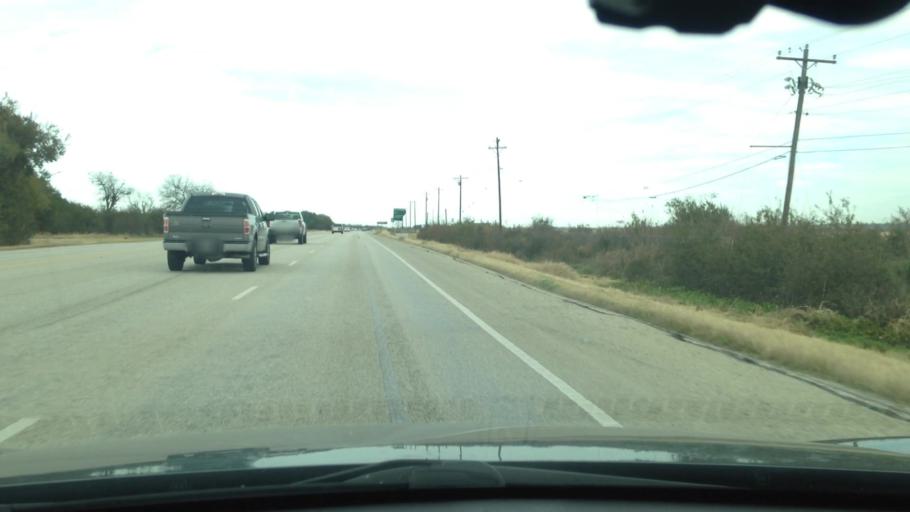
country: US
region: Texas
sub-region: Hays County
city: San Marcos
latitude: 29.8926
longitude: -97.8821
